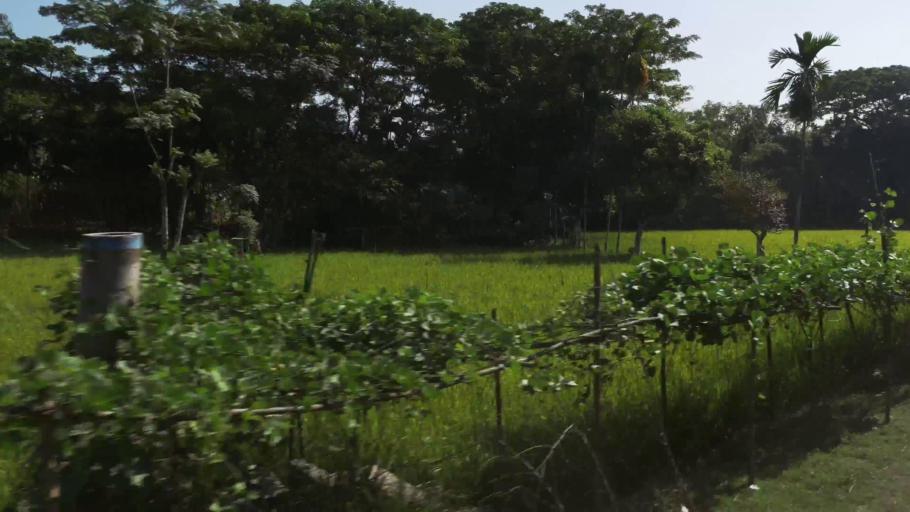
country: BD
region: Dhaka
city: Gafargaon
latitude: 24.5352
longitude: 90.5086
